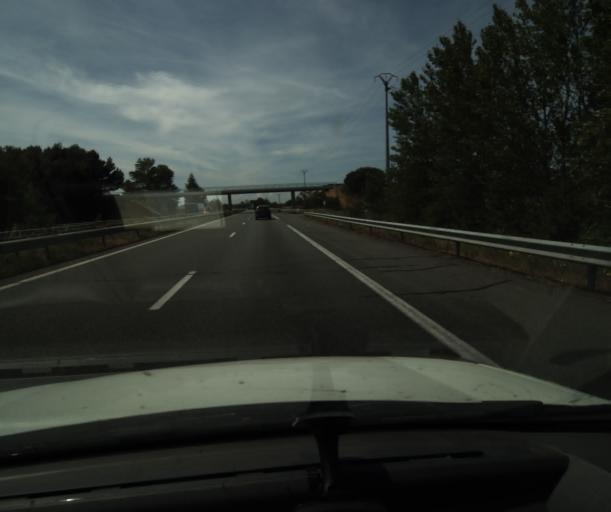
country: FR
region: Languedoc-Roussillon
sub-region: Departement de l'Aude
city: Villepinte
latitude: 43.2477
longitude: 2.0668
